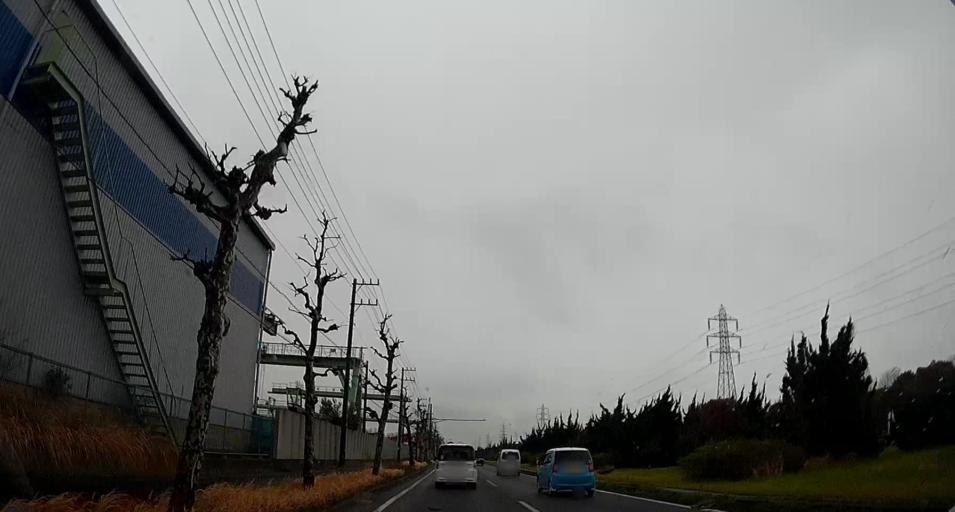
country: JP
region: Chiba
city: Ichihara
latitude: 35.5148
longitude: 140.0584
